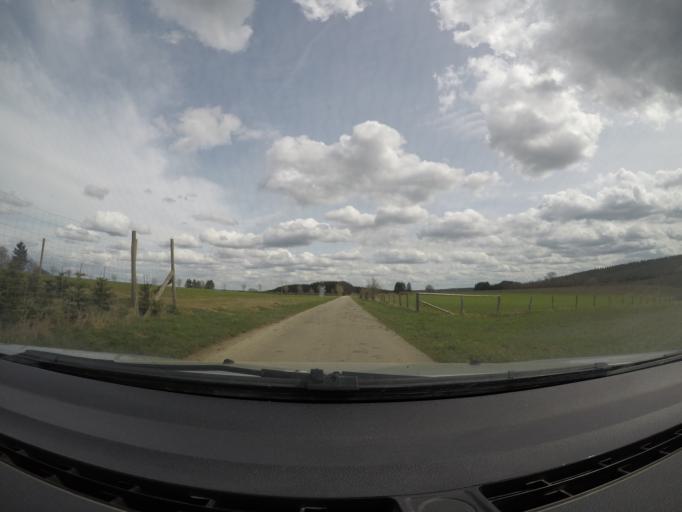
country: BE
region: Wallonia
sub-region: Province du Luxembourg
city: Leglise
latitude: 49.7967
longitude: 5.4830
